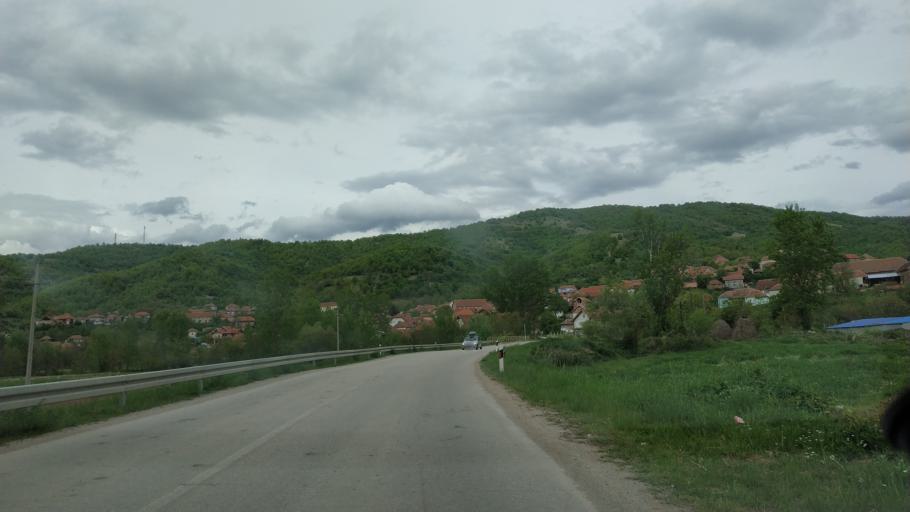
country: RS
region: Central Serbia
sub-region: Nisavski Okrug
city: Aleksinac
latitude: 43.6317
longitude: 21.7157
